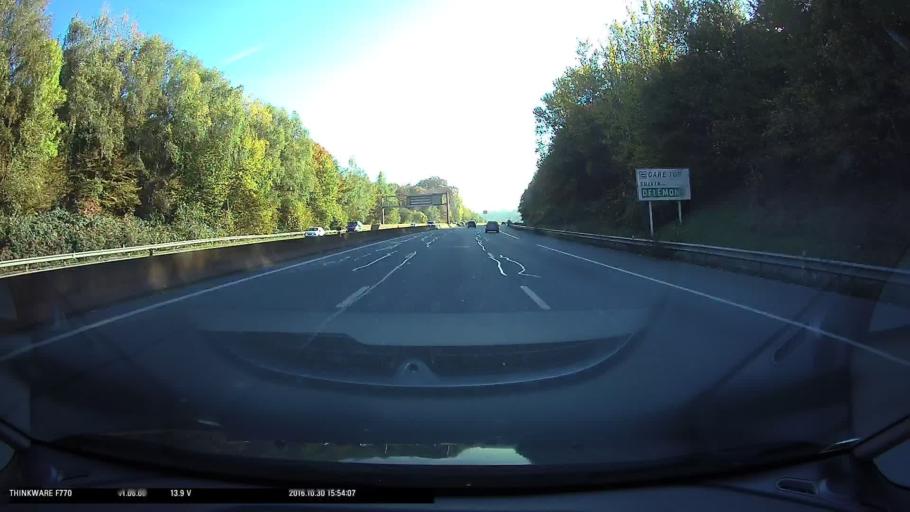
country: FR
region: Franche-Comte
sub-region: Territoire de Belfort
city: Andelnans
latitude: 47.6049
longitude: 6.8568
